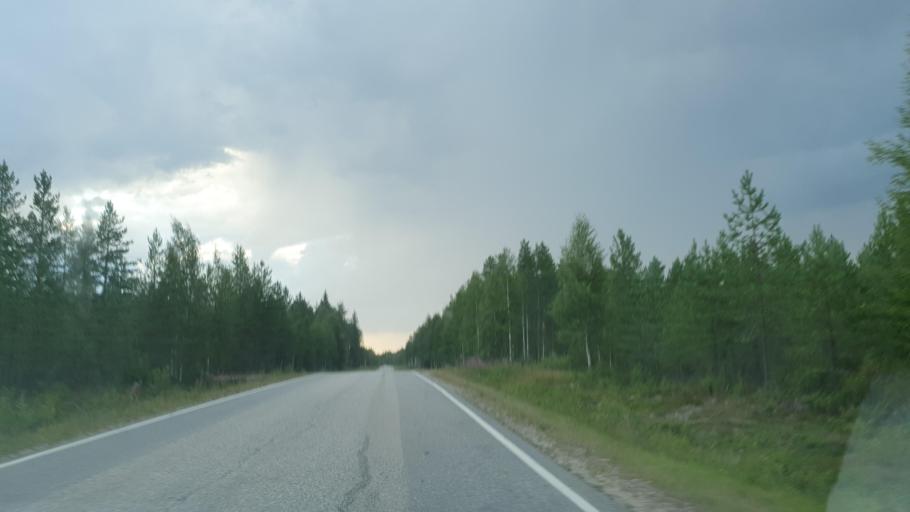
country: FI
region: Kainuu
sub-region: Kehys-Kainuu
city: Kuhmo
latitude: 64.3006
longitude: 29.1308
